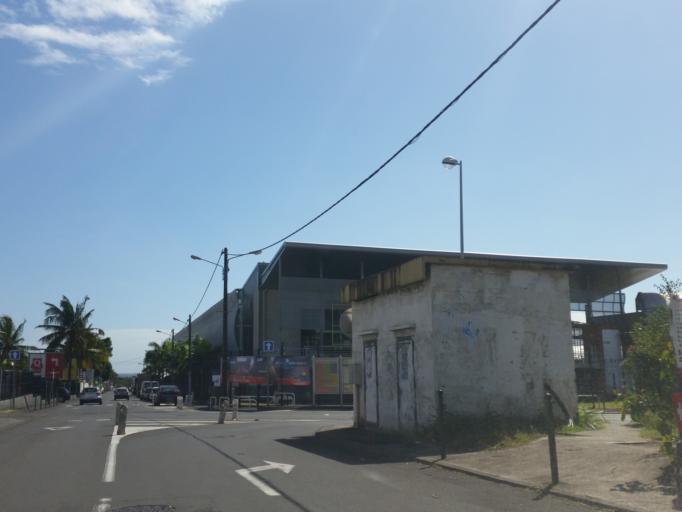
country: RE
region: Reunion
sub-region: Reunion
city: Saint-Denis
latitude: -20.8950
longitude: 55.4976
